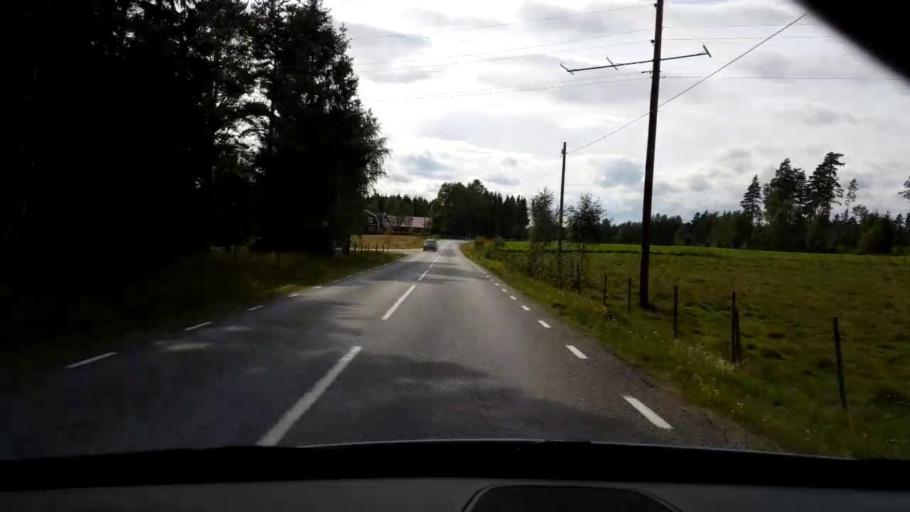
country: SE
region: Joenkoeping
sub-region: Vetlanda Kommun
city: Landsbro
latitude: 57.3795
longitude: 14.9930
